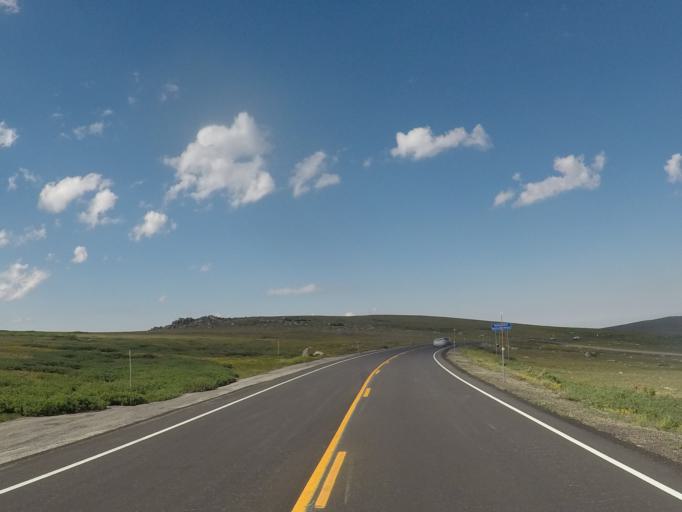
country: US
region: Montana
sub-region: Carbon County
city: Red Lodge
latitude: 45.0072
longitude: -109.4083
